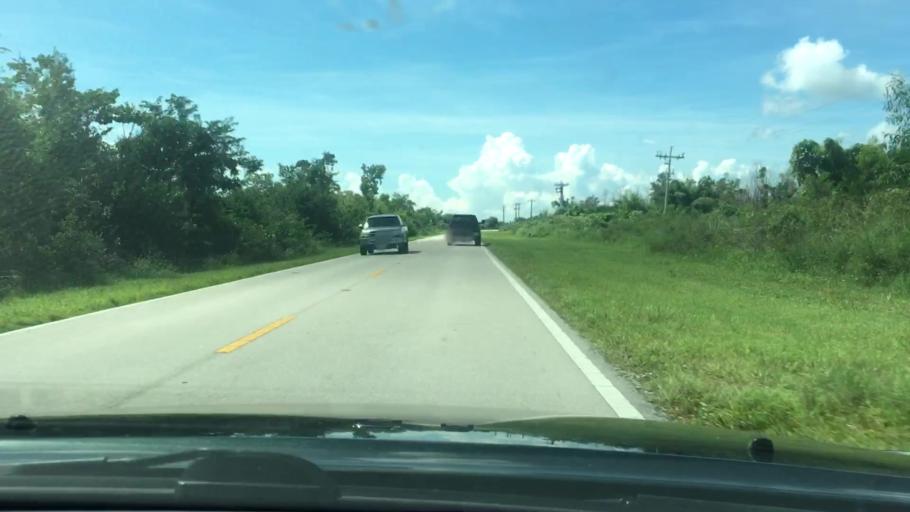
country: US
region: Florida
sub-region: Collier County
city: Marco
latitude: 25.9383
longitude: -81.6469
